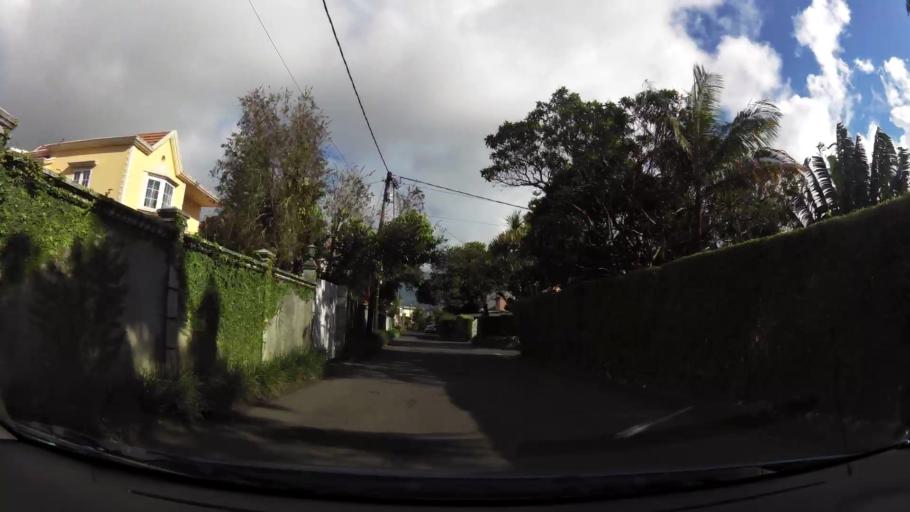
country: MU
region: Plaines Wilhems
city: Curepipe
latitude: -20.3254
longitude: 57.5186
